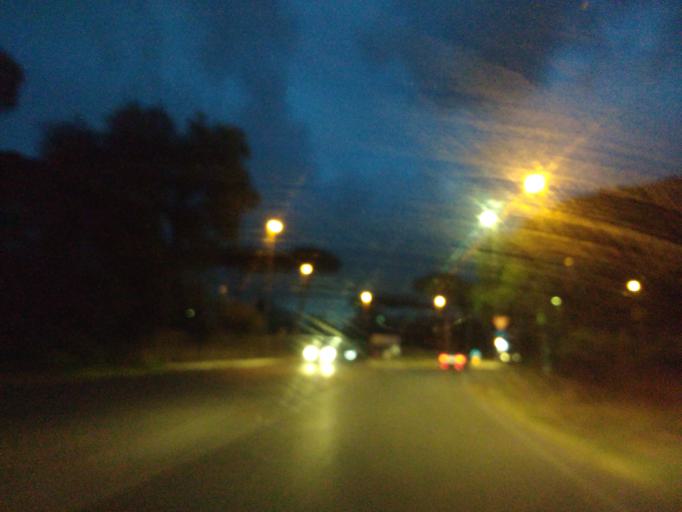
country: IT
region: Latium
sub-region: Citta metropolitana di Roma Capitale
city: Anzio
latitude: 41.4633
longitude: 12.6218
